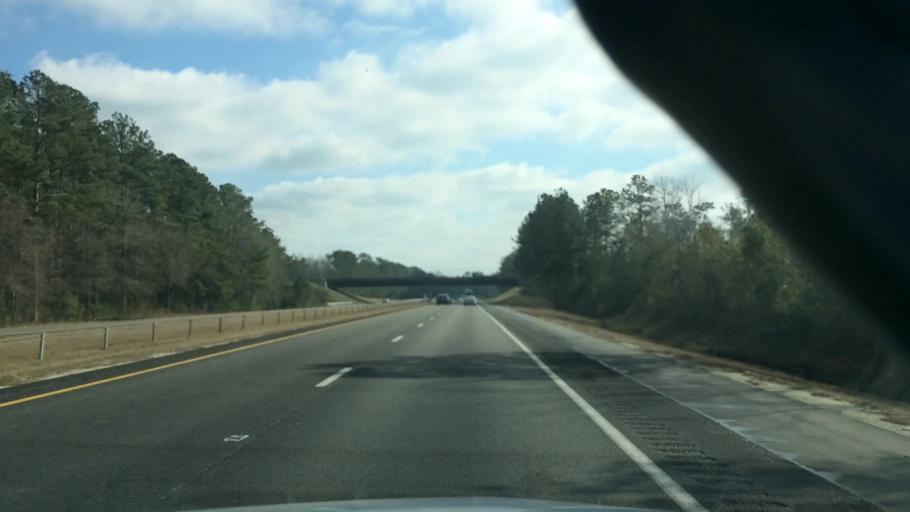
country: US
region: North Carolina
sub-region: Pender County
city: Burgaw
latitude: 34.6138
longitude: -77.9223
